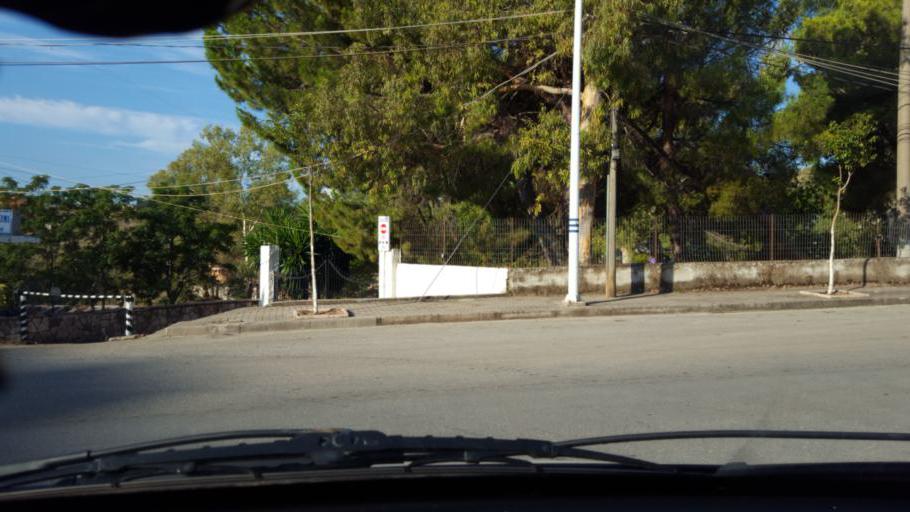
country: AL
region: Vlore
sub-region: Rrethi i Sarandes
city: Sarande
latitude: 39.8750
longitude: 19.9875
